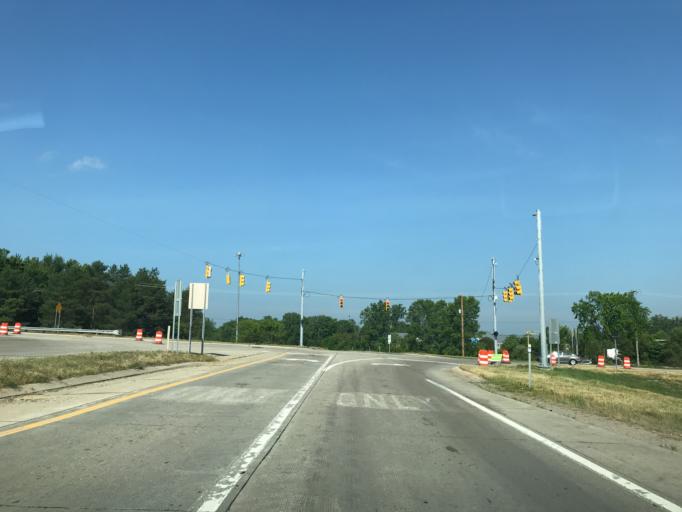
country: US
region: Michigan
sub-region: Ingham County
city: Okemos
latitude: 42.6799
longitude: -84.4322
